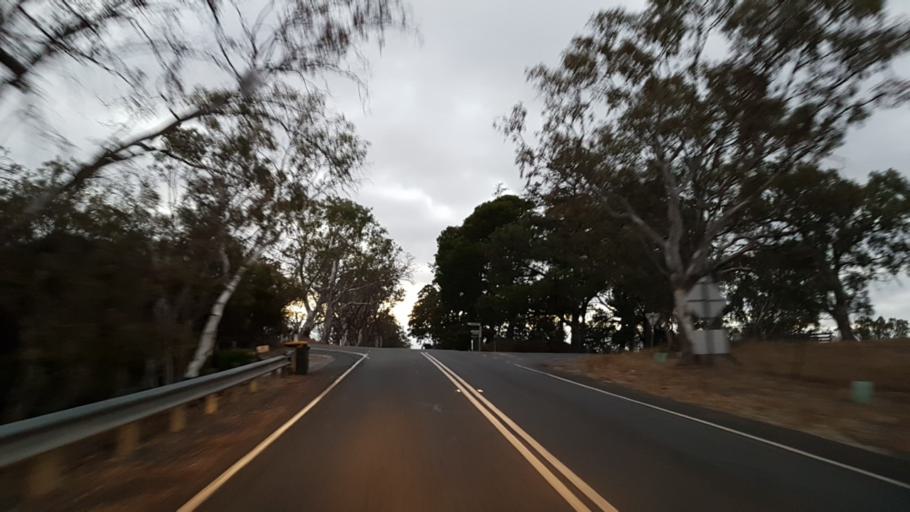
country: AU
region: South Australia
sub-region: Mount Barker
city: Nairne
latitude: -35.0318
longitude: 138.9543
